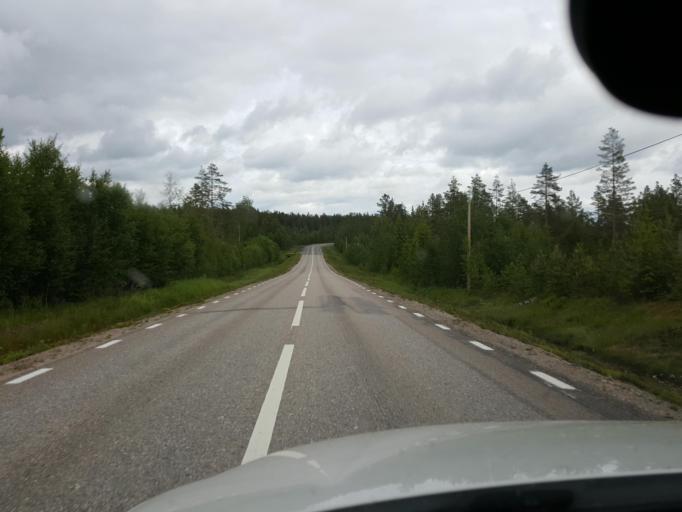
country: SE
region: Gaevleborg
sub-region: Ljusdals Kommun
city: Farila
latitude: 61.7604
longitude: 15.4848
